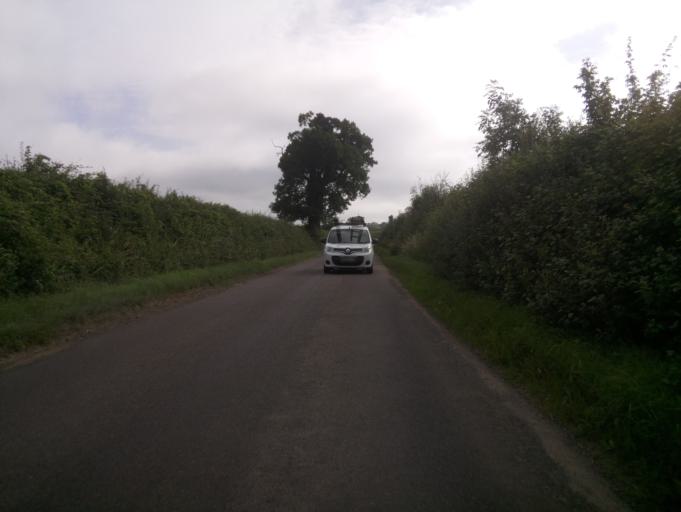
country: GB
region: England
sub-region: Borough of Swindon
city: Hannington
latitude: 51.6178
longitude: -1.7462
